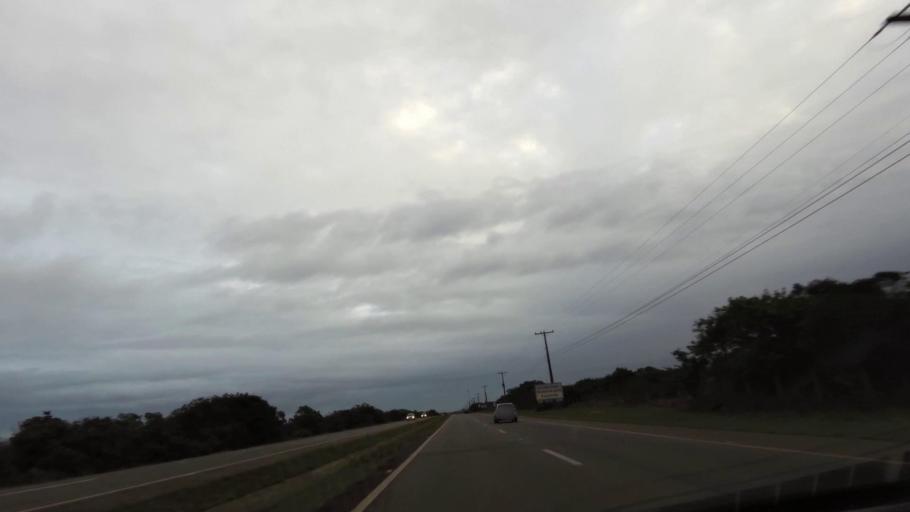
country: BR
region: Espirito Santo
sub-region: Guarapari
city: Guarapari
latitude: -20.5667
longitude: -40.4101
